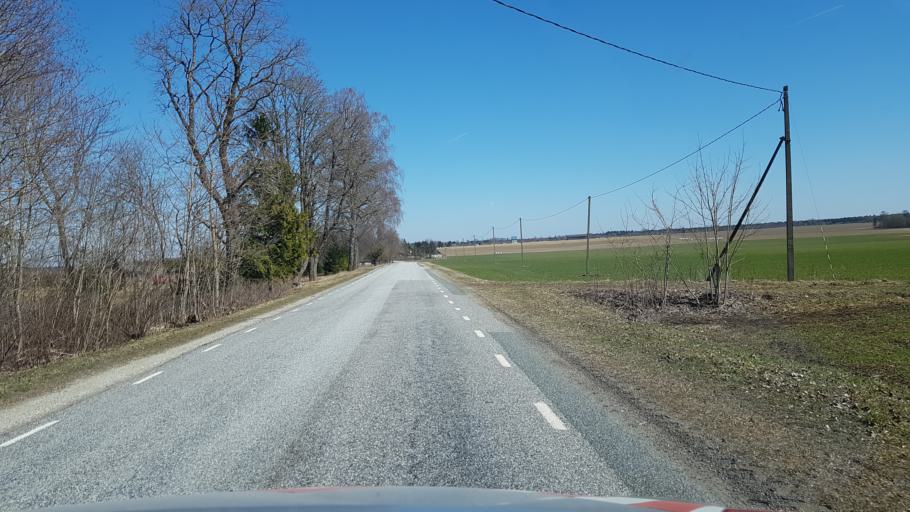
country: EE
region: Jaervamaa
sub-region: Koeru vald
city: Koeru
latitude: 59.0477
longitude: 26.0579
